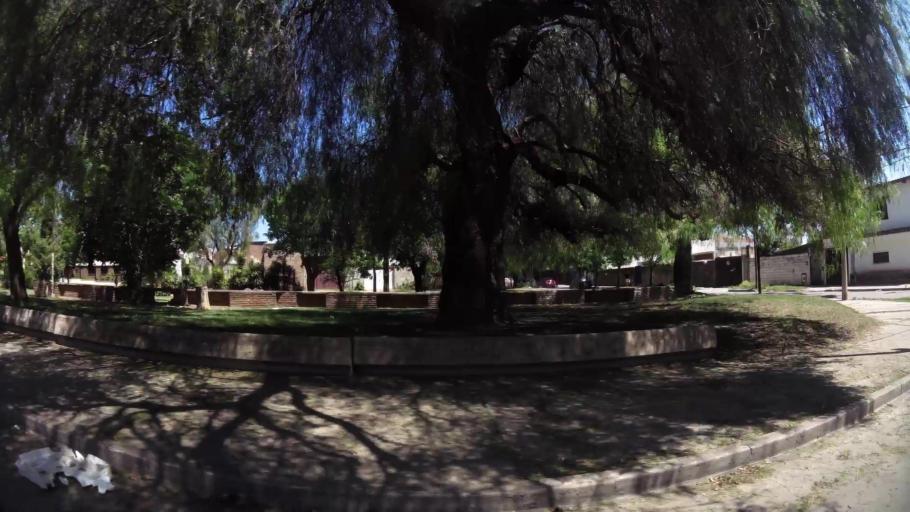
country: AR
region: Cordoba
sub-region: Departamento de Capital
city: Cordoba
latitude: -31.4115
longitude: -64.2131
